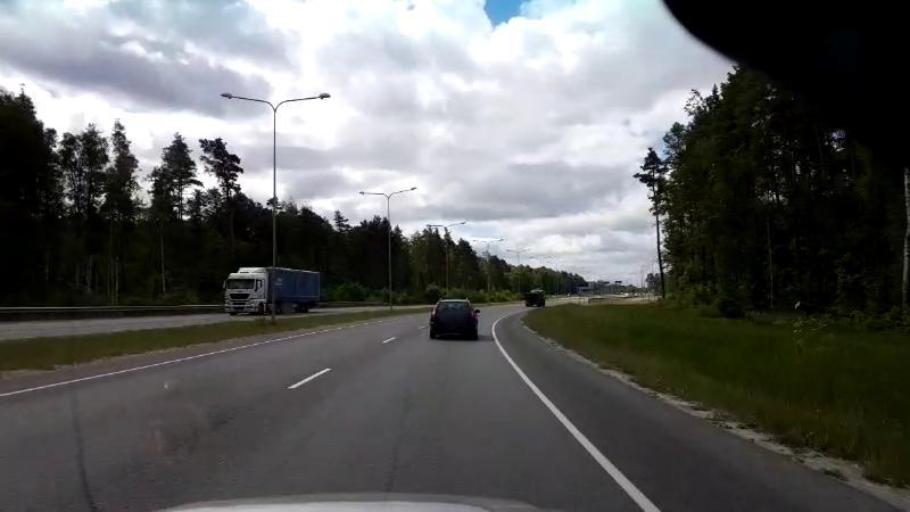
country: EE
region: Paernumaa
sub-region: Paernu linn
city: Parnu
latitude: 58.3829
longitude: 24.5566
